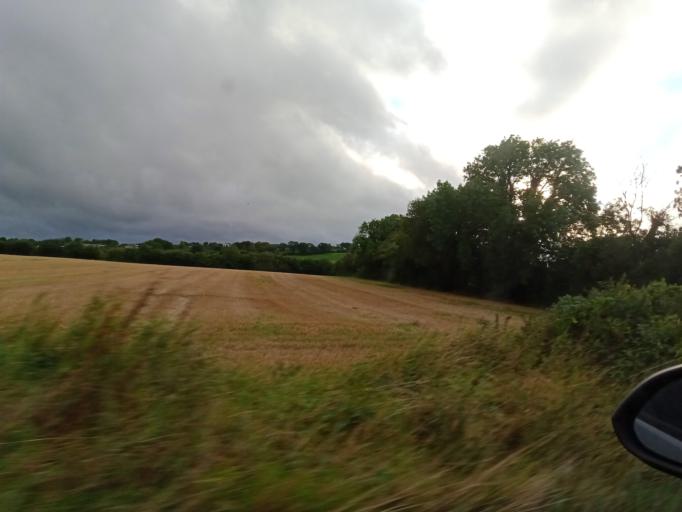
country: IE
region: Leinster
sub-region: Laois
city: Mountmellick
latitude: 53.1332
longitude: -7.3984
